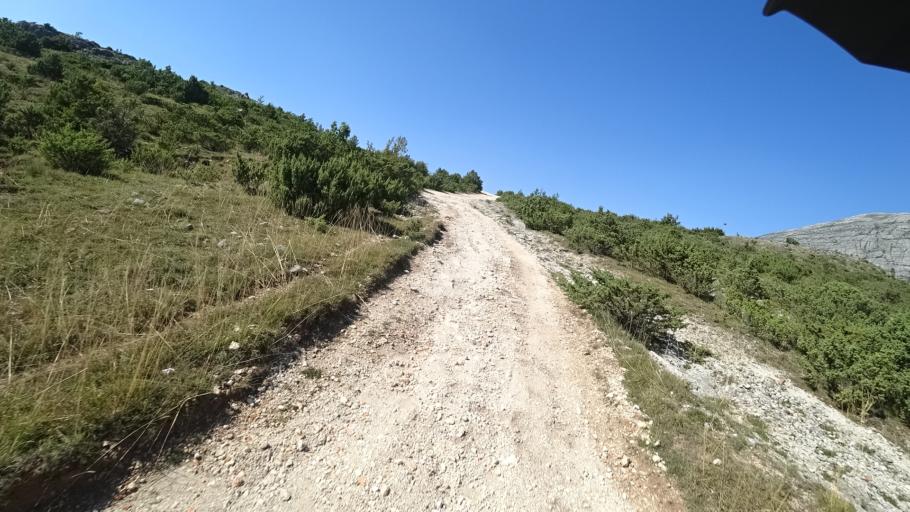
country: HR
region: Splitsko-Dalmatinska
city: Hrvace
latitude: 43.9381
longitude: 16.4586
